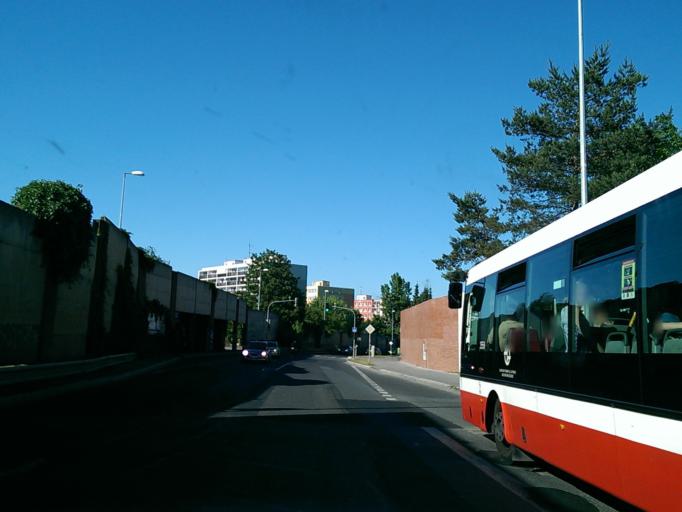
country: CZ
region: Central Bohemia
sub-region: Okres Praha-Zapad
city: Pruhonice
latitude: 50.0447
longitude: 14.5190
